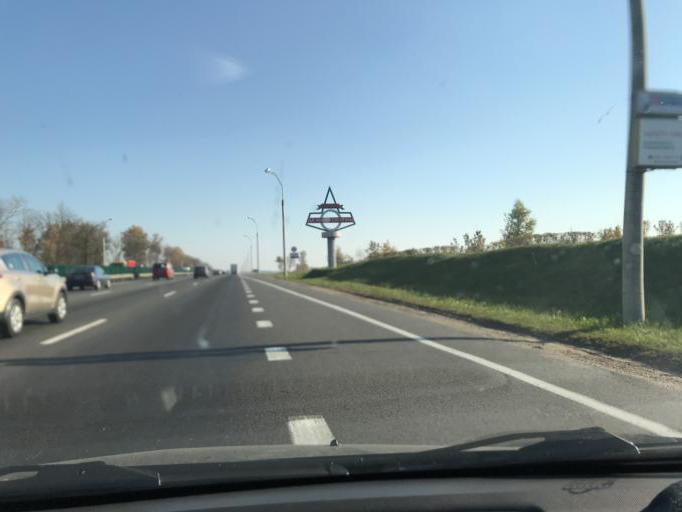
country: BY
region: Minsk
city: Vyaliki Trastsyanets
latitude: 53.8426
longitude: 27.7167
